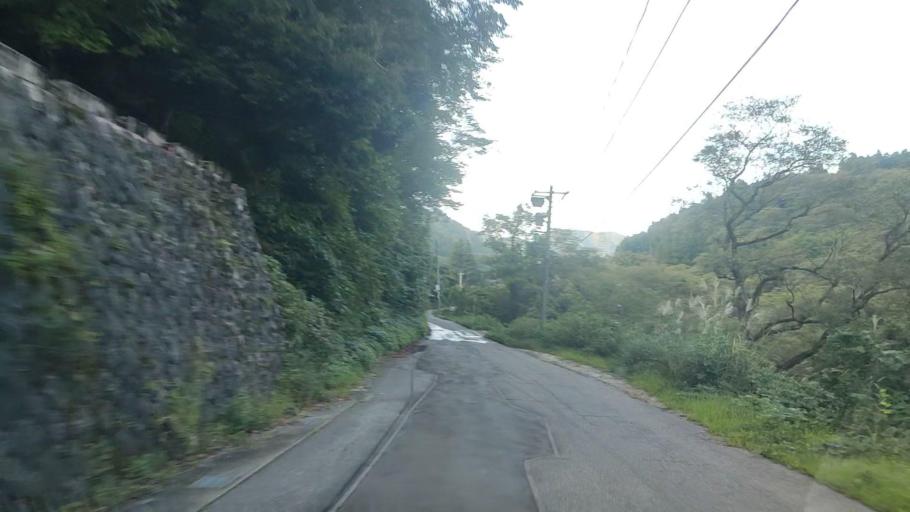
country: JP
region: Toyama
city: Yatsuomachi-higashikumisaka
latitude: 36.4895
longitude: 137.0640
